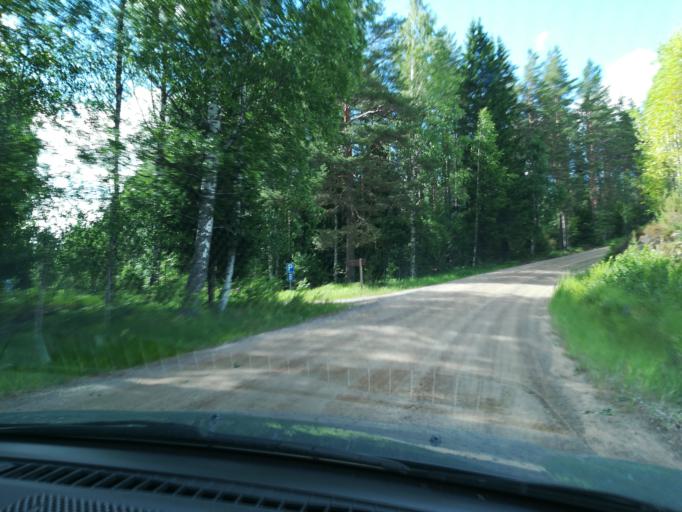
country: FI
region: South Karelia
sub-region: Lappeenranta
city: Savitaipale
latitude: 61.3014
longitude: 27.6377
